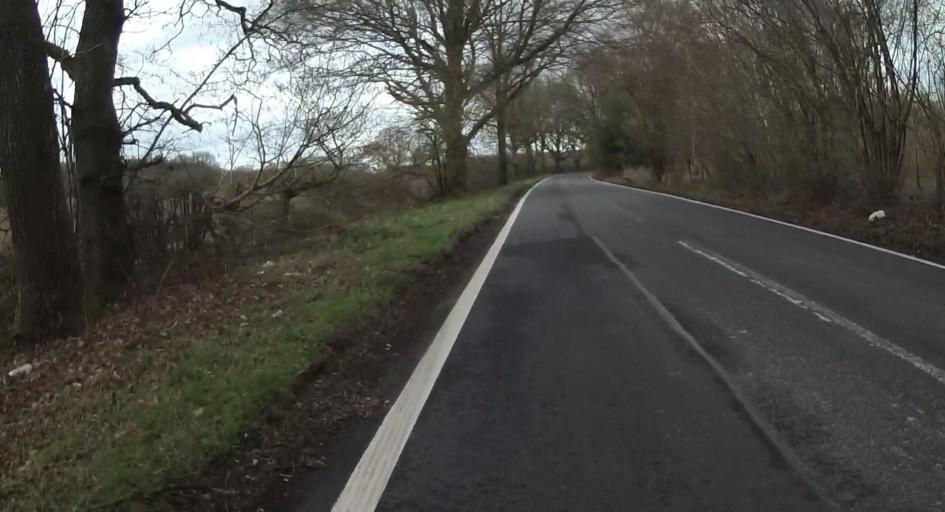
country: GB
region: England
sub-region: Hampshire
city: Old Basing
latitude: 51.1904
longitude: -1.0394
